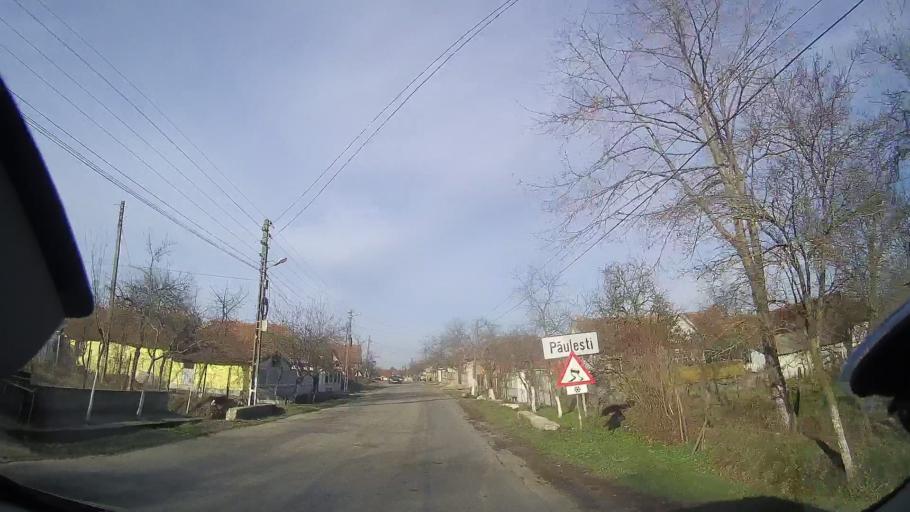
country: RO
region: Bihor
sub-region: Comuna Brusturi
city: Brusturi
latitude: 47.1687
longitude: 22.2202
